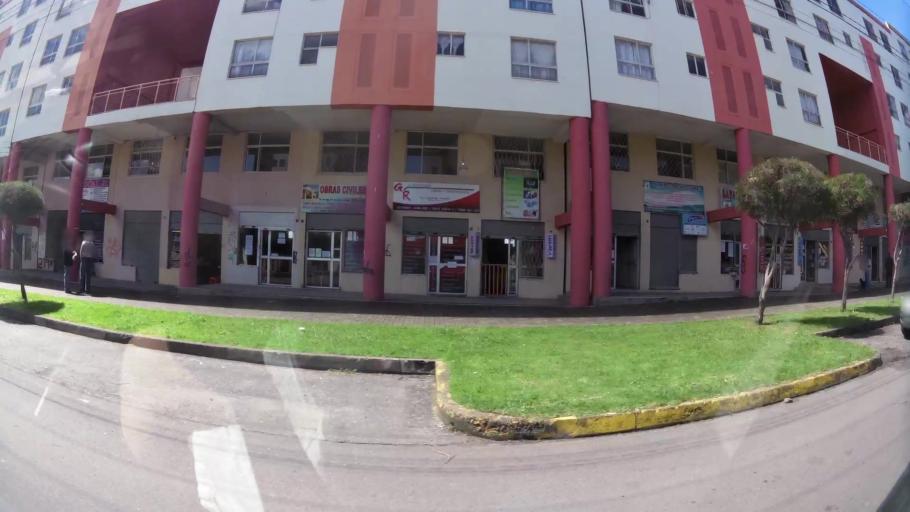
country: EC
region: Pichincha
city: Quito
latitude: -0.2950
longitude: -78.5485
